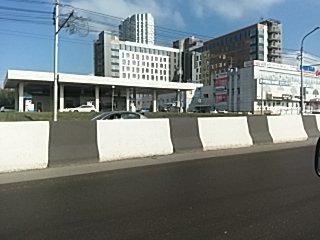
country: RU
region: Krasnoyarskiy
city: Krasnoyarsk
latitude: 56.0340
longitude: 92.9247
